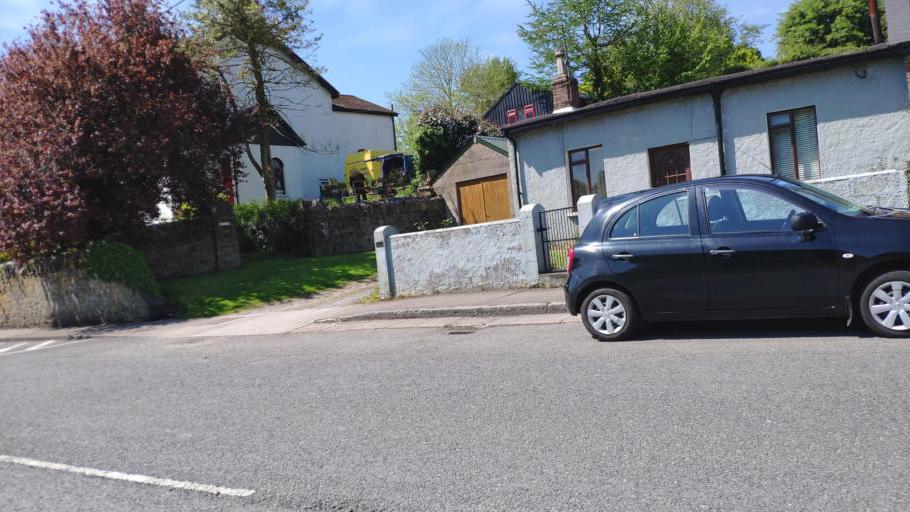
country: IE
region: Munster
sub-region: County Cork
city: Blarney
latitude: 51.9350
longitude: -8.5629
